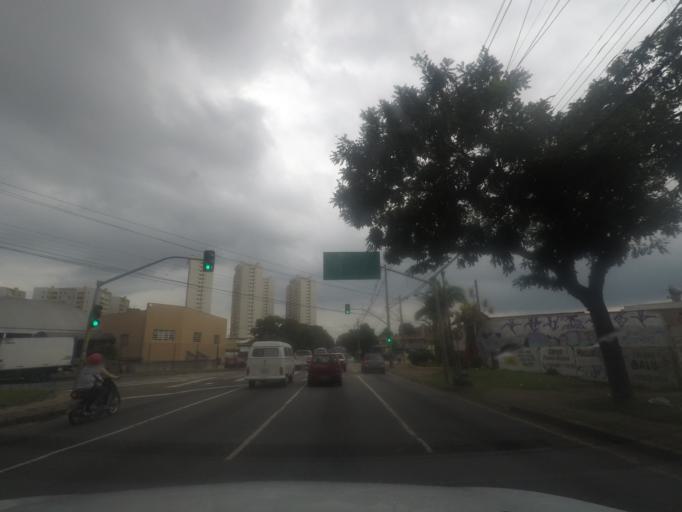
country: BR
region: Parana
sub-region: Curitiba
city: Curitiba
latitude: -25.4961
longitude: -49.2961
